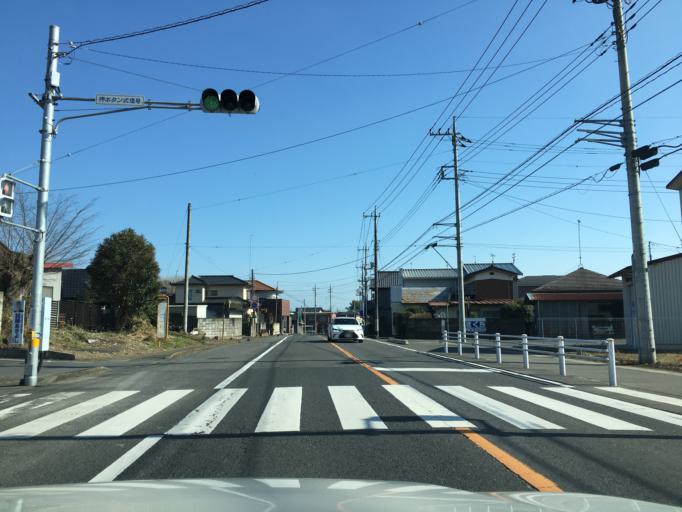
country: JP
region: Ibaraki
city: Omiya
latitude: 36.5178
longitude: 140.3642
